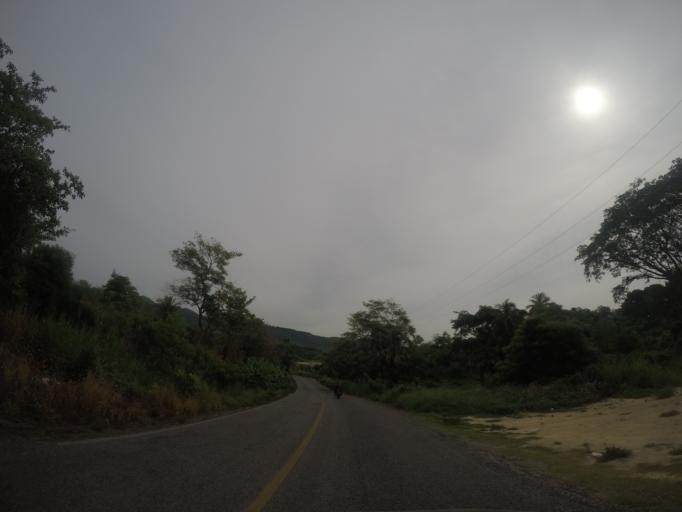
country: MX
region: Oaxaca
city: San Pedro Mixtepec
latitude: 15.9311
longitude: -97.1517
